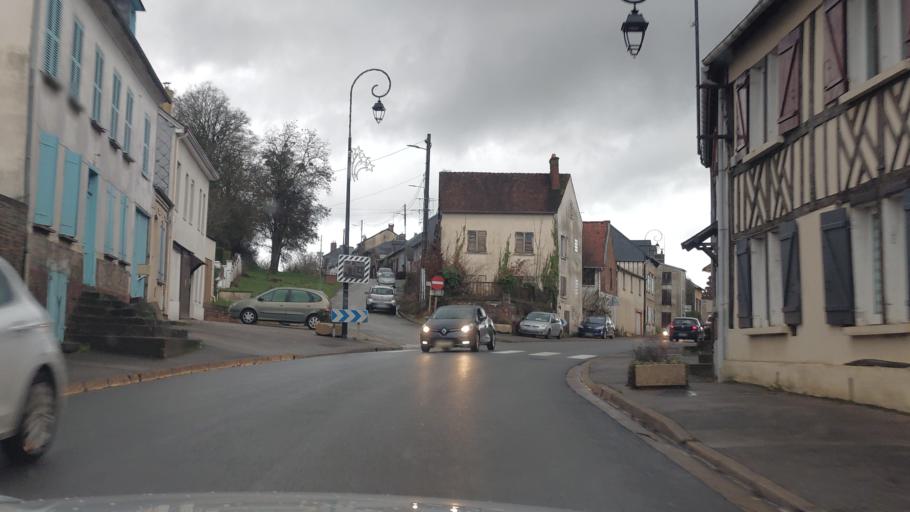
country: FR
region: Picardie
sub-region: Departement de l'Oise
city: Saint-Omer-en-Chaussee
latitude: 49.5770
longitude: 1.9542
